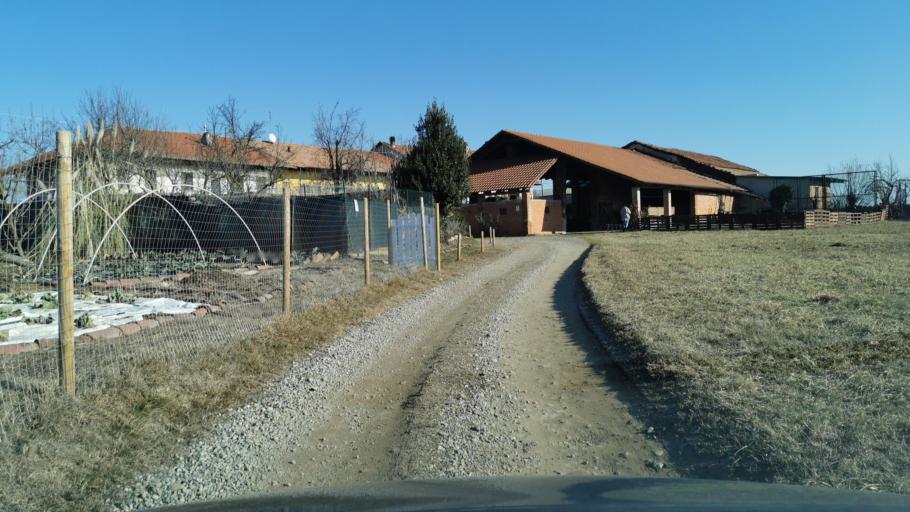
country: IT
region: Piedmont
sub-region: Provincia di Torino
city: Leini
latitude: 45.2149
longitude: 7.6947
